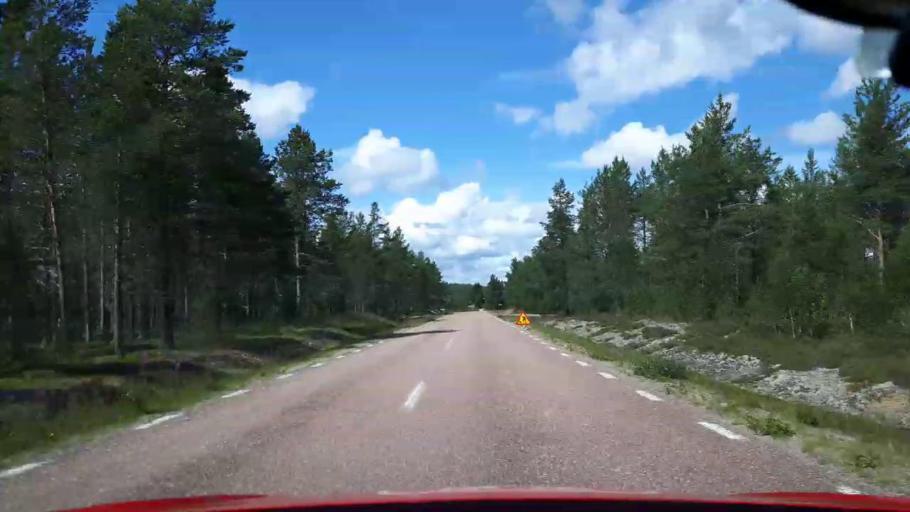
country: SE
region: Dalarna
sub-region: Alvdalens Kommun
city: AElvdalen
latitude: 61.8205
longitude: 13.5744
